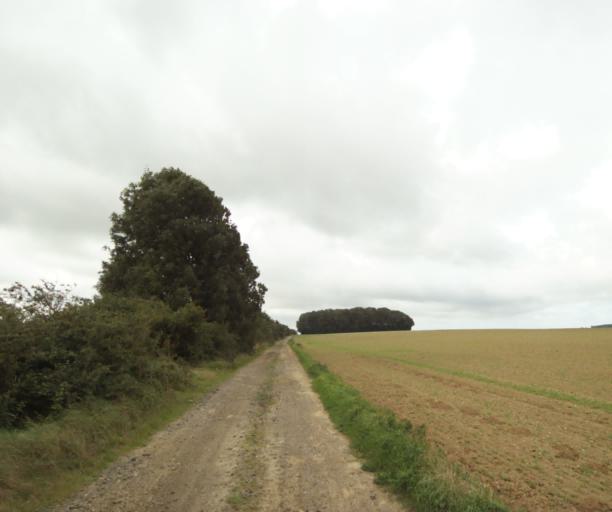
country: FR
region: Nord-Pas-de-Calais
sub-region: Departement du Pas-de-Calais
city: Etaples
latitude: 50.5300
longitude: 1.6710
